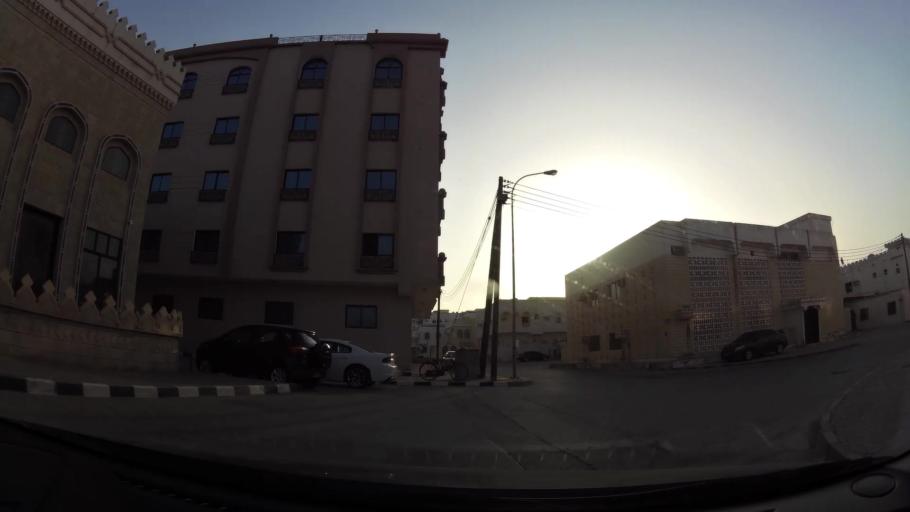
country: OM
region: Zufar
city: Salalah
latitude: 17.0135
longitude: 54.1086
